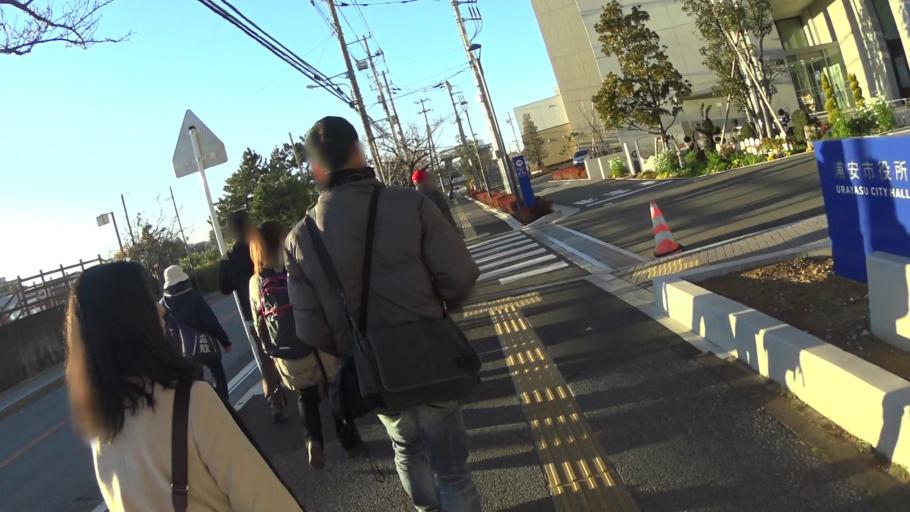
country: JP
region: Tokyo
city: Urayasu
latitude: 35.6526
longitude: 139.9019
